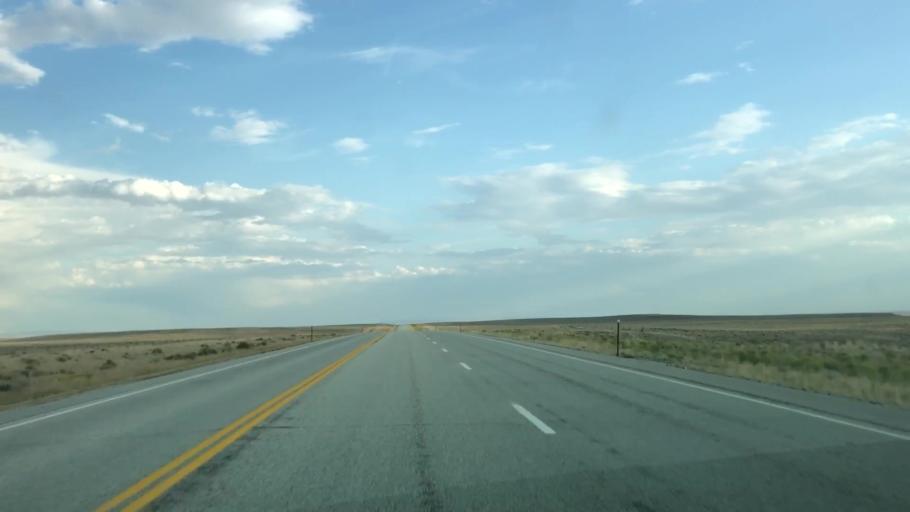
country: US
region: Wyoming
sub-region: Sweetwater County
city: North Rock Springs
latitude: 42.2757
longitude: -109.4821
